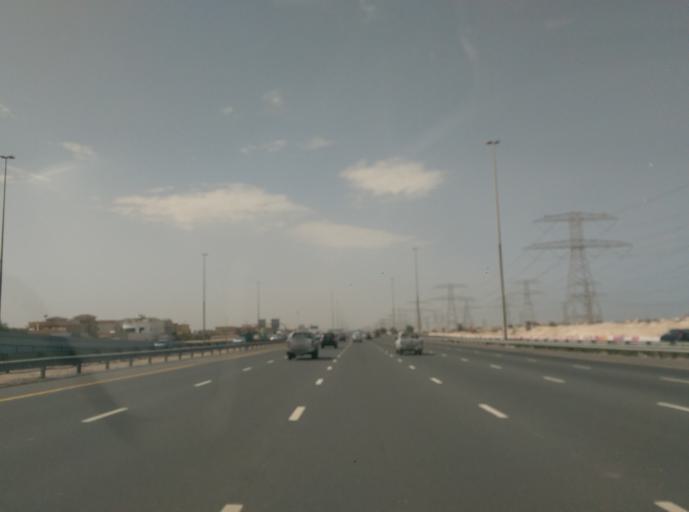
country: AE
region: Dubai
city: Dubai
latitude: 25.1006
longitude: 55.2315
